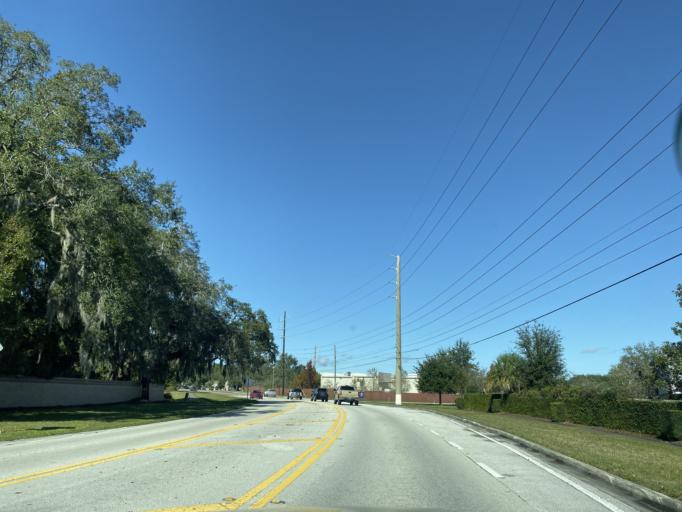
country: US
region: Florida
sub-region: Seminole County
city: Goldenrod
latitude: 28.6178
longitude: -81.2469
